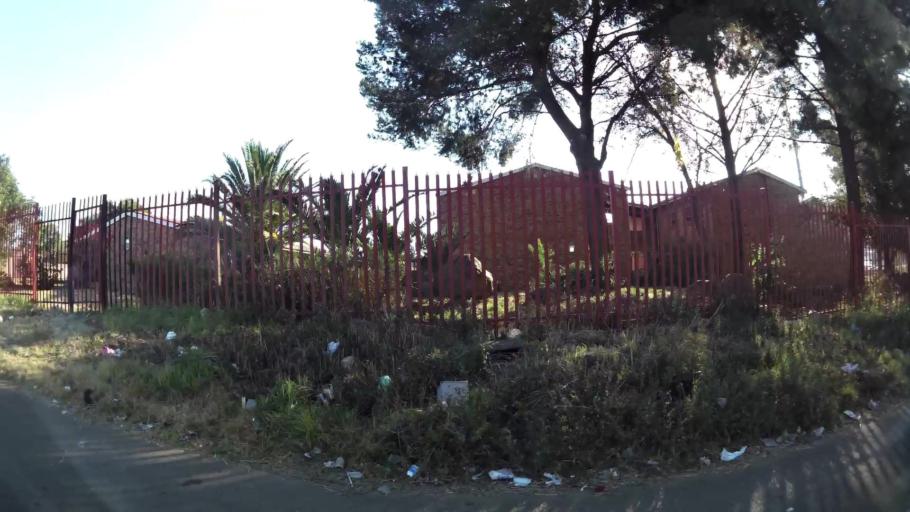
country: ZA
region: Gauteng
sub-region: City of Johannesburg Metropolitan Municipality
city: Soweto
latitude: -26.2673
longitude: 27.8678
